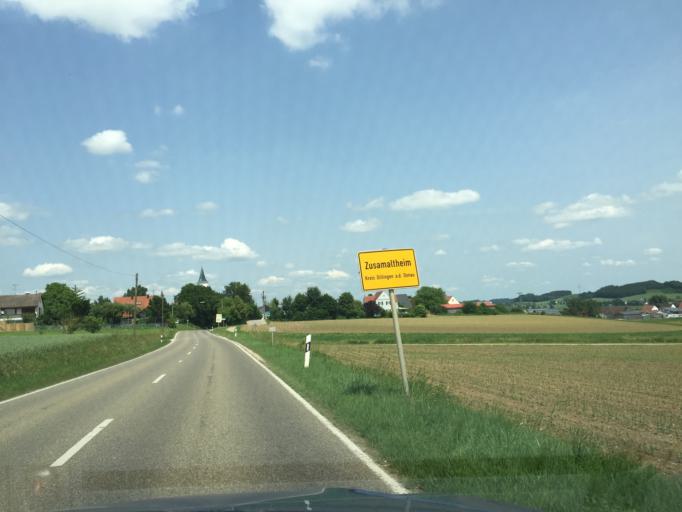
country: DE
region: Bavaria
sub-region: Swabia
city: Zusamaltheim
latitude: 48.5272
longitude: 10.6324
